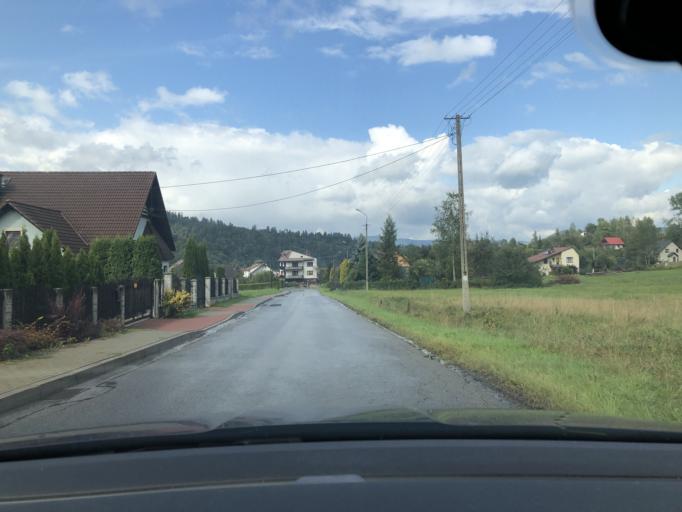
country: PL
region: Lesser Poland Voivodeship
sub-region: Powiat suski
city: Stryszawa
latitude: 49.7101
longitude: 19.5285
